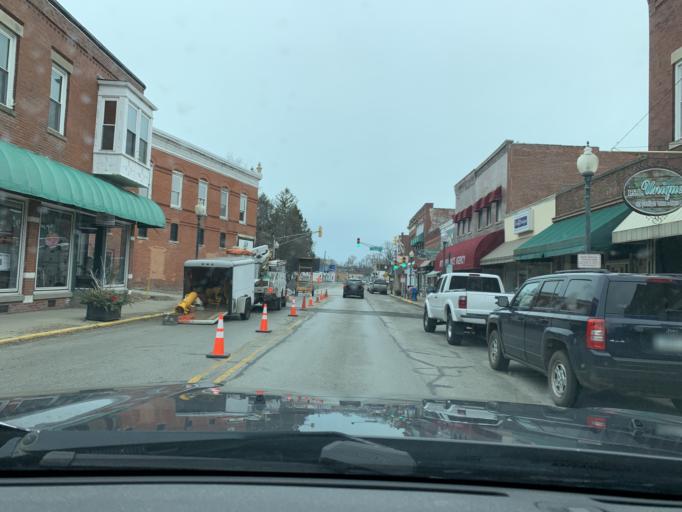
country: US
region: Indiana
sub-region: Porter County
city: Chesterton
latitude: 41.6102
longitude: -87.0521
